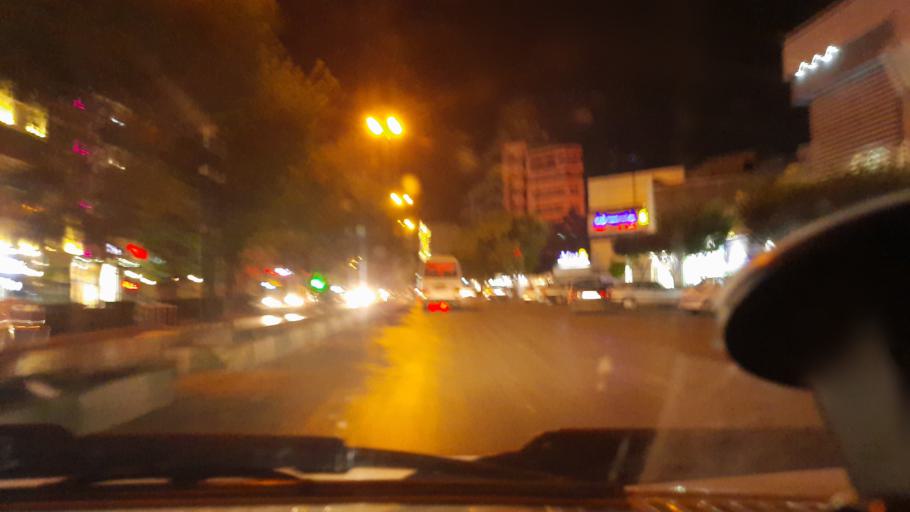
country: IR
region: Markazi
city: Arak
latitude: 34.0791
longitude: 49.7000
